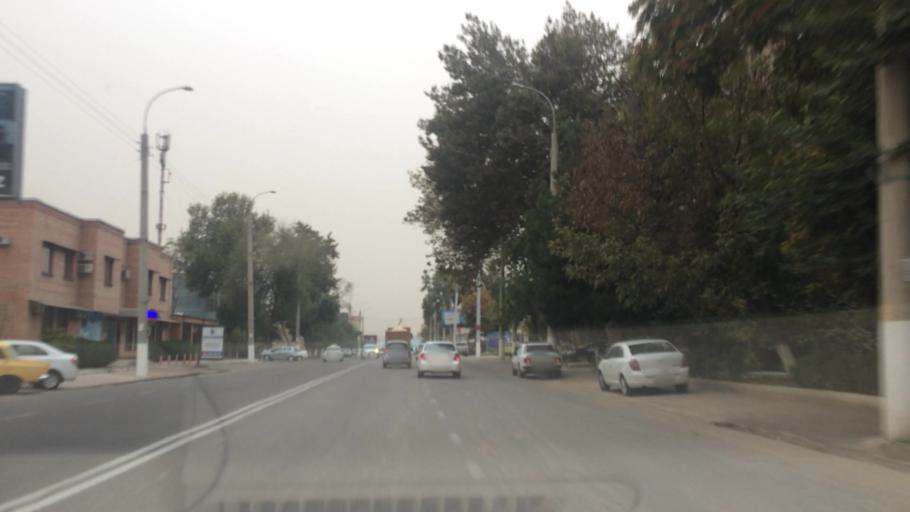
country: UZ
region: Toshkent Shahri
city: Tashkent
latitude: 41.3060
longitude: 69.2514
